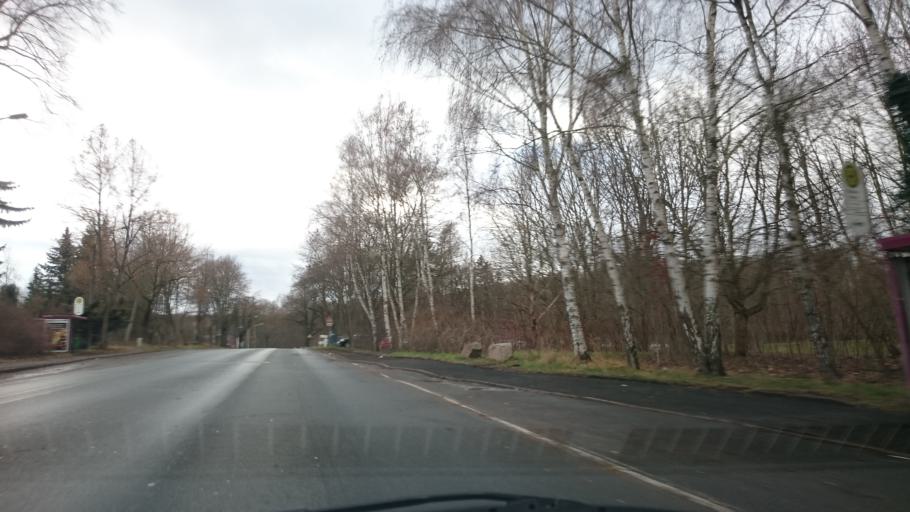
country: DE
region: Saxony
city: Wilkau-Hasslau
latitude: 50.6960
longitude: 12.4966
